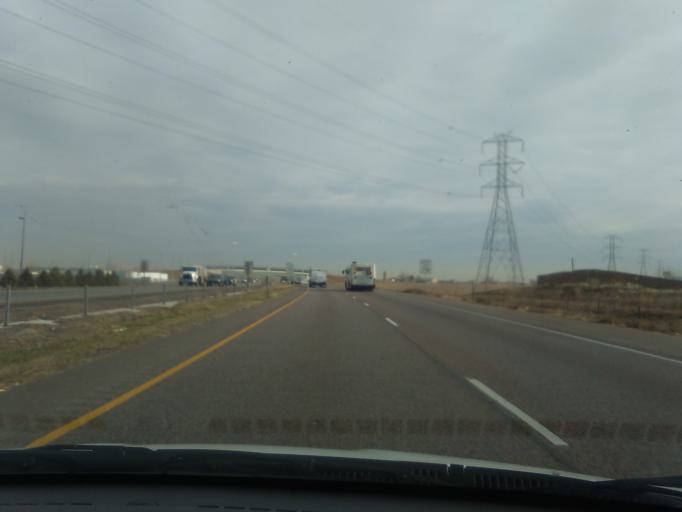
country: US
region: Colorado
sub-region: Adams County
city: Derby
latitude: 39.8827
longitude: -104.8738
